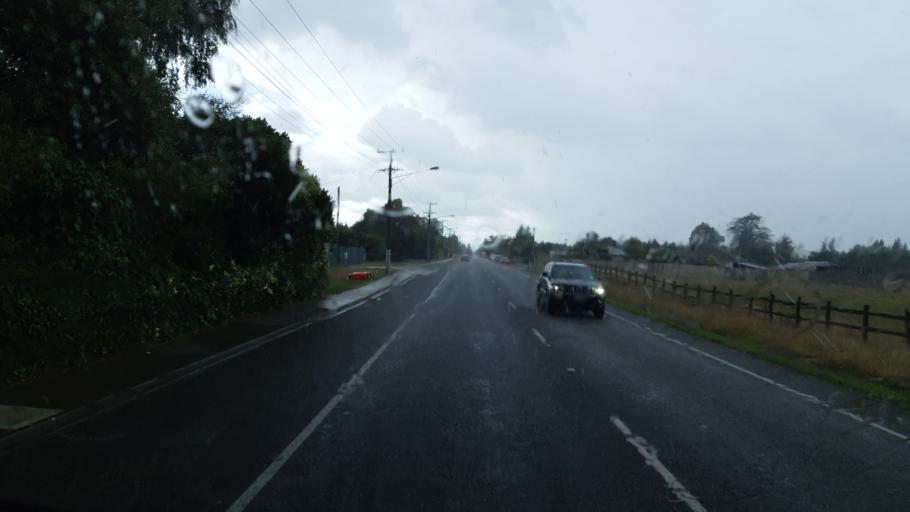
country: NZ
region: Tasman
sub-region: Tasman District
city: Wakefield
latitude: -41.4011
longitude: 173.0568
